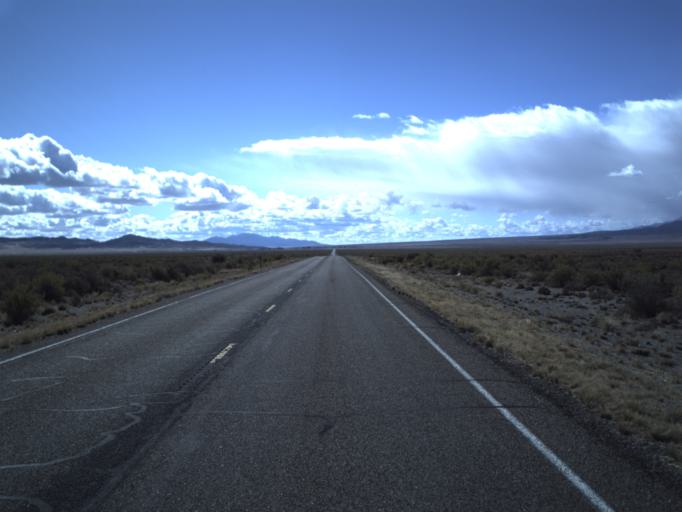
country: US
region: Nevada
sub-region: White Pine County
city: McGill
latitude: 39.0427
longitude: -114.0362
